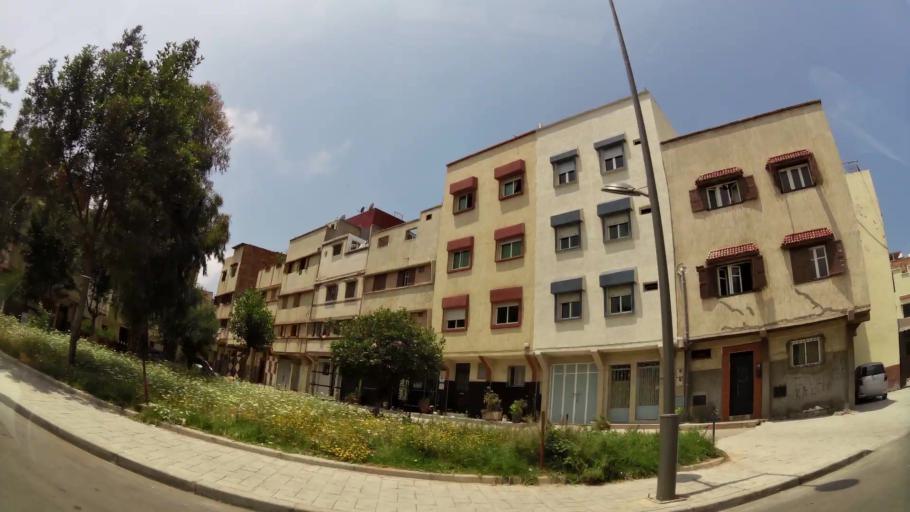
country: MA
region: Rabat-Sale-Zemmour-Zaer
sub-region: Rabat
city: Rabat
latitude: 33.9871
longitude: -6.8775
